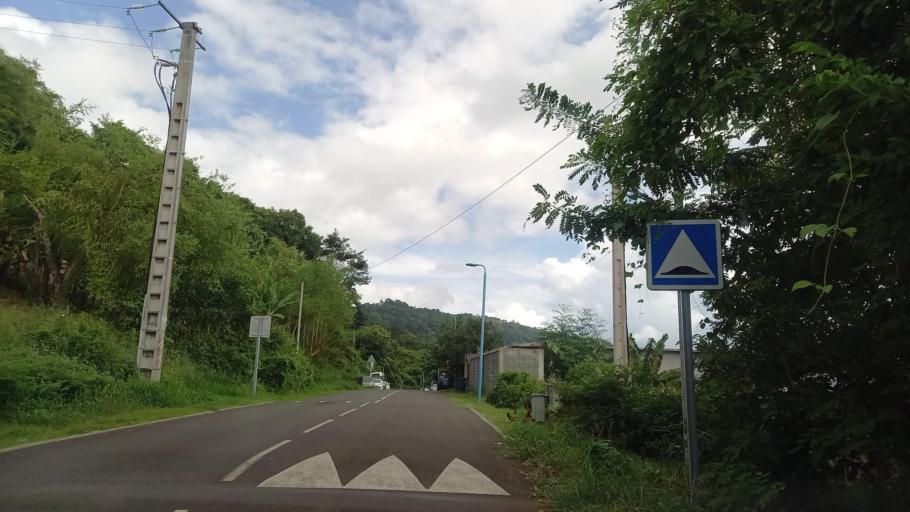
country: YT
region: Kani-Keli
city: Kani Keli
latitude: -12.9436
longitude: 45.1025
